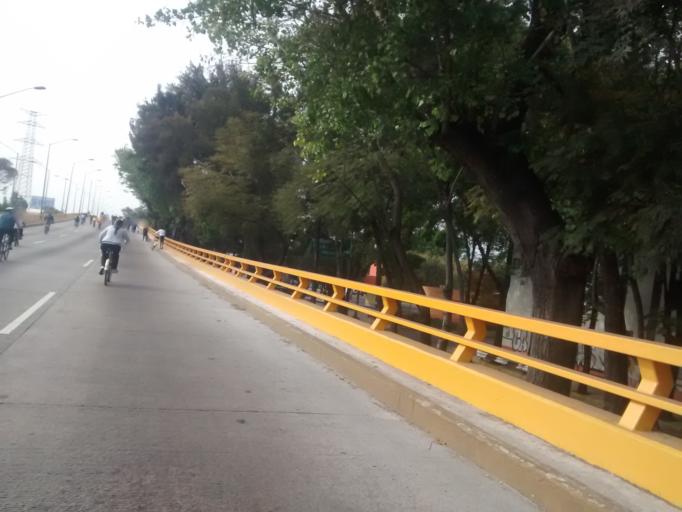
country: MX
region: Mexico City
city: Colonia Nativitas
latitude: 19.3623
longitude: -99.1291
